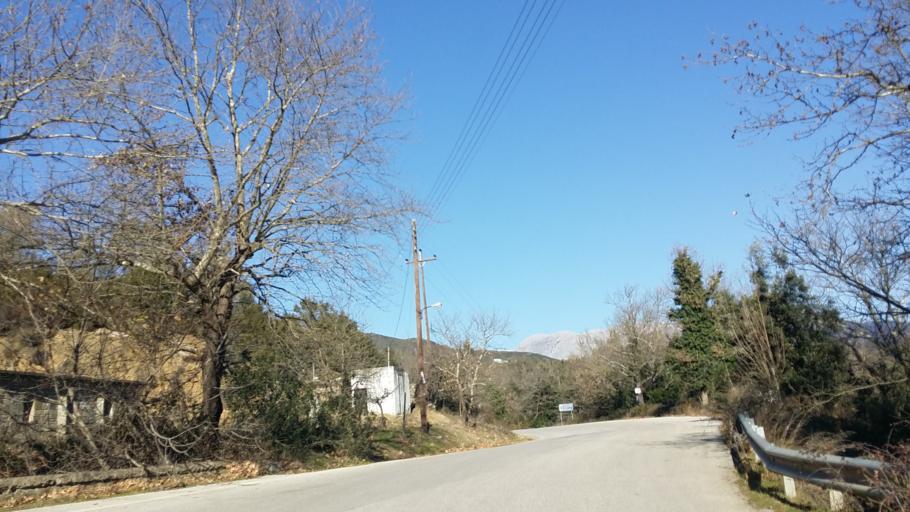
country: GR
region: West Greece
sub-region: Nomos Aitolias kai Akarnanias
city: Sardinia
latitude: 38.8992
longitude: 21.3486
